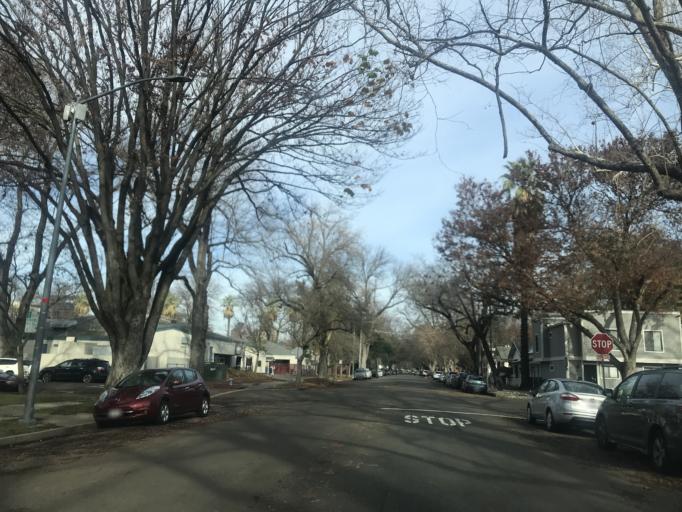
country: US
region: California
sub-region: Sacramento County
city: Sacramento
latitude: 38.5661
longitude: -121.4967
